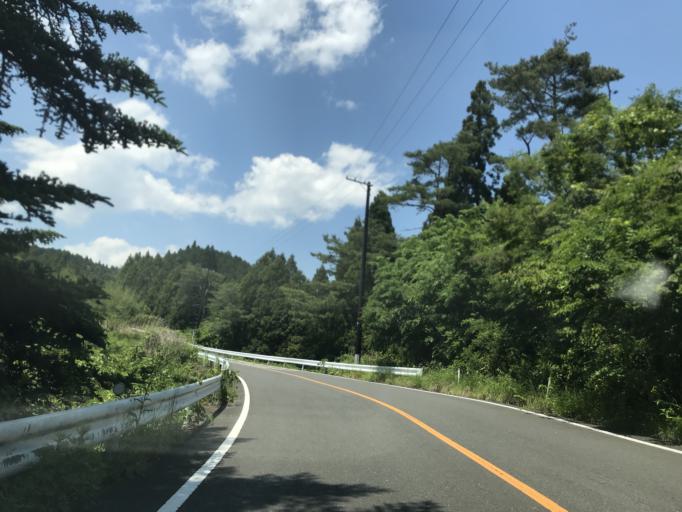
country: JP
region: Miyagi
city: Matsushima
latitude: 38.3613
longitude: 141.0527
